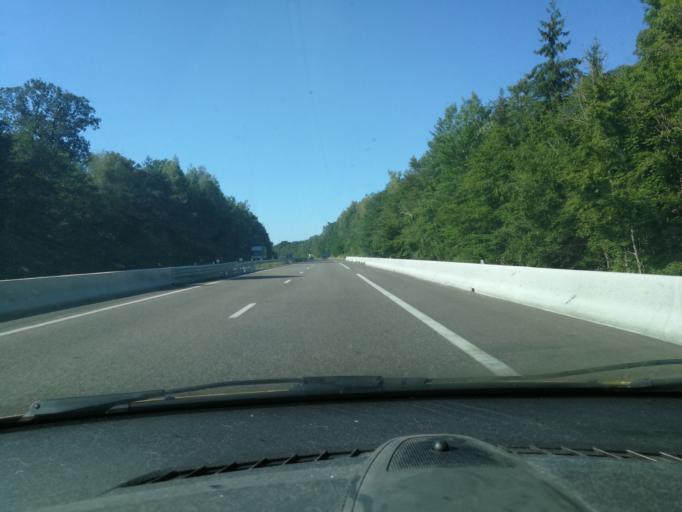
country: FR
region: Alsace
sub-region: Departement du Bas-Rhin
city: Herbitzheim
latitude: 48.9973
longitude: 7.0659
